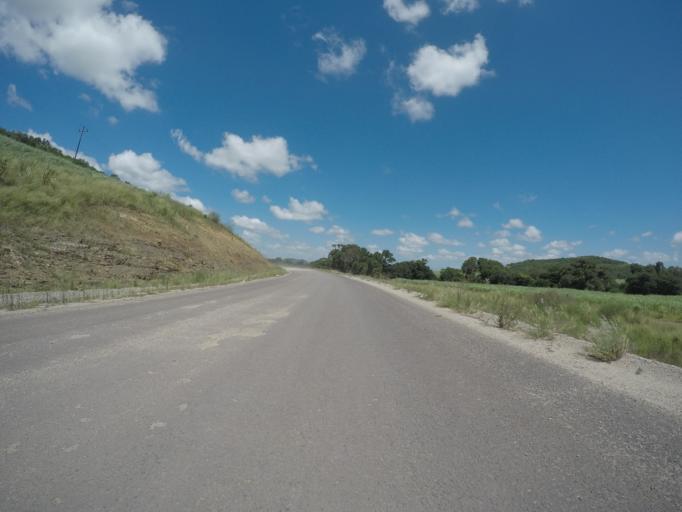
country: ZA
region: KwaZulu-Natal
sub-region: uThungulu District Municipality
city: Empangeni
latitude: -28.6541
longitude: 31.7689
